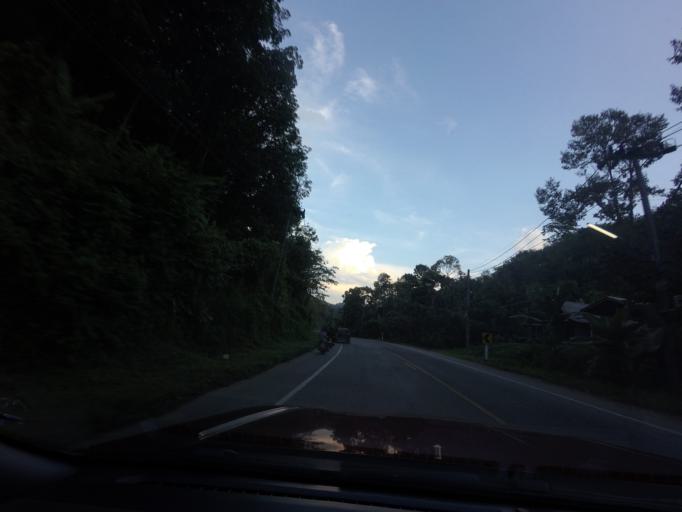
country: TH
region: Yala
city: Than To
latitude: 6.0967
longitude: 101.1799
